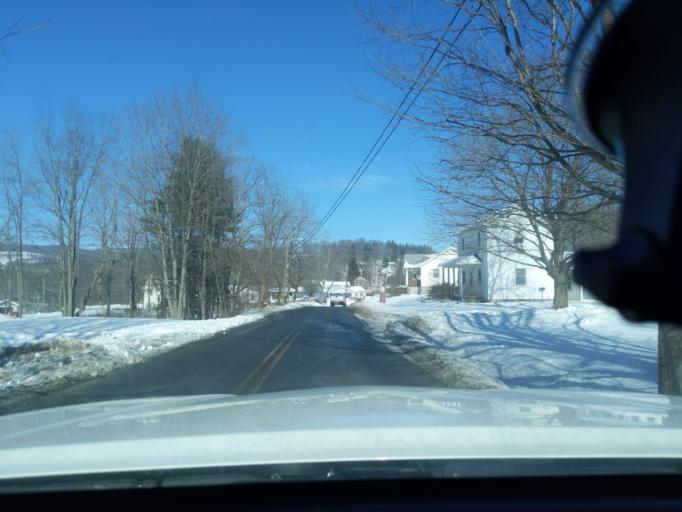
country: US
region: Maryland
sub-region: Allegany County
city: Frostburg
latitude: 39.6375
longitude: -78.9289
